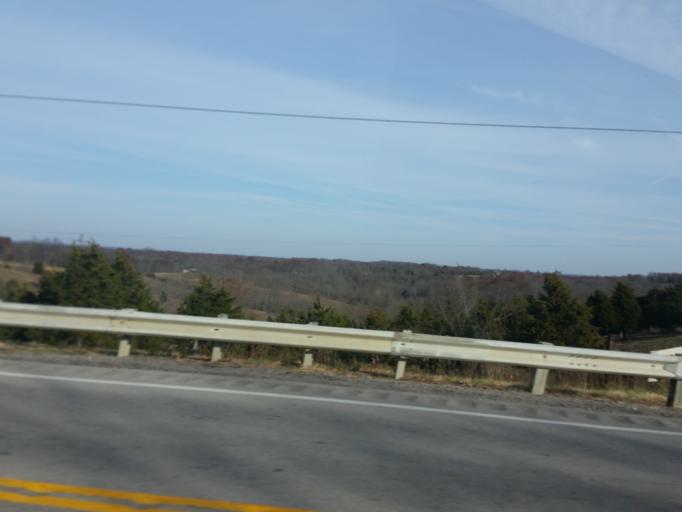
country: US
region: Kentucky
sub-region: Pendleton County
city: Falmouth
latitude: 38.5536
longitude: -84.2896
